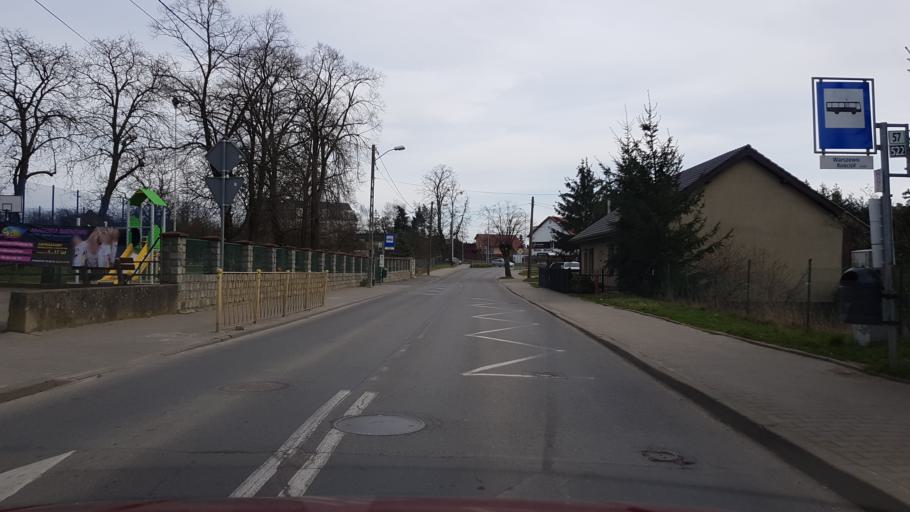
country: PL
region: West Pomeranian Voivodeship
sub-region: Szczecin
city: Szczecin
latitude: 53.4726
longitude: 14.5474
